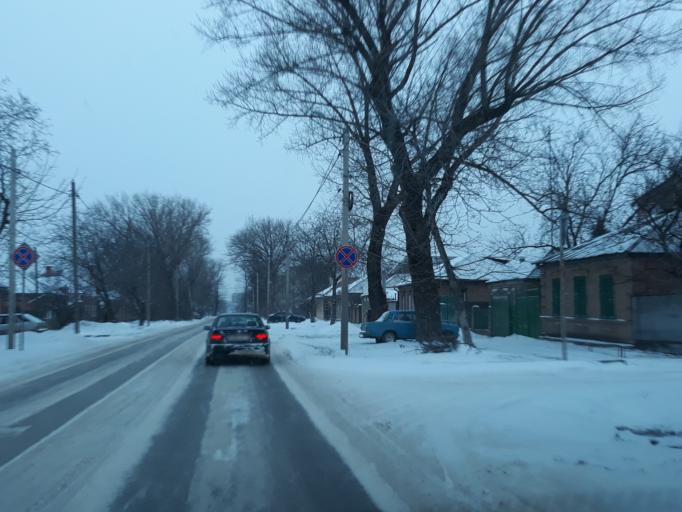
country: RU
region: Rostov
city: Taganrog
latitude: 47.2626
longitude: 38.9356
